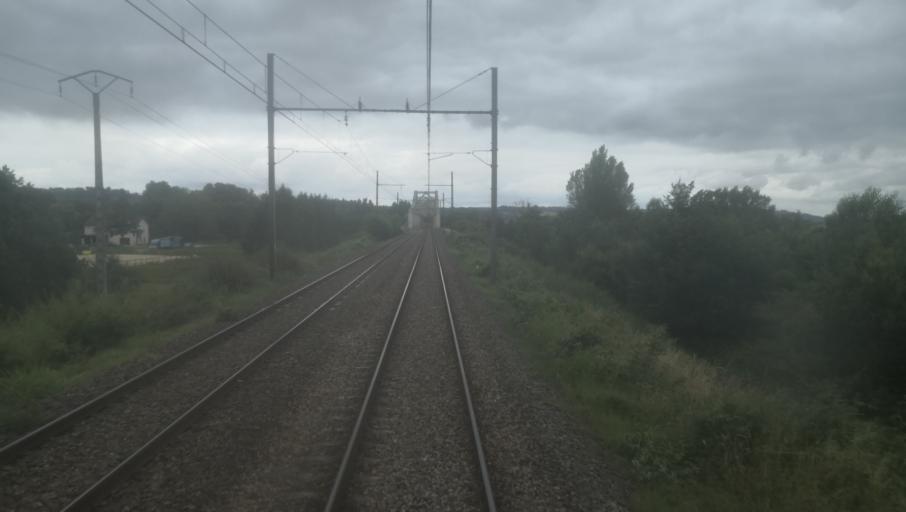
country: FR
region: Midi-Pyrenees
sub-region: Departement du Tarn-et-Garonne
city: Moissac
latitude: 44.0880
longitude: 1.1042
